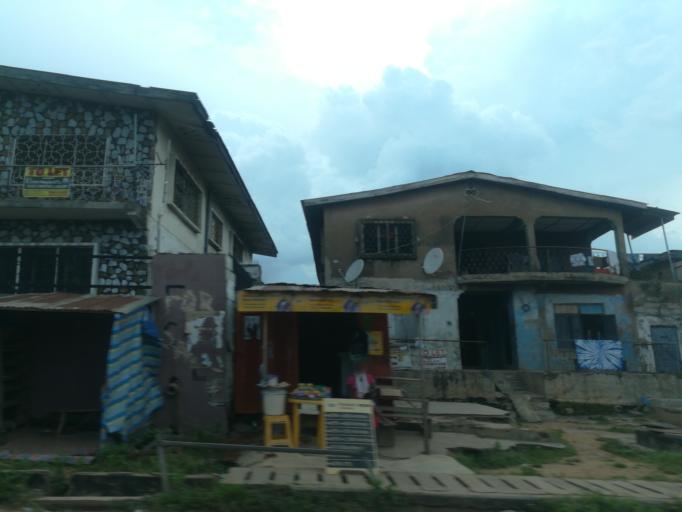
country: NG
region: Oyo
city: Ibadan
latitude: 7.4260
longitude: 3.8960
